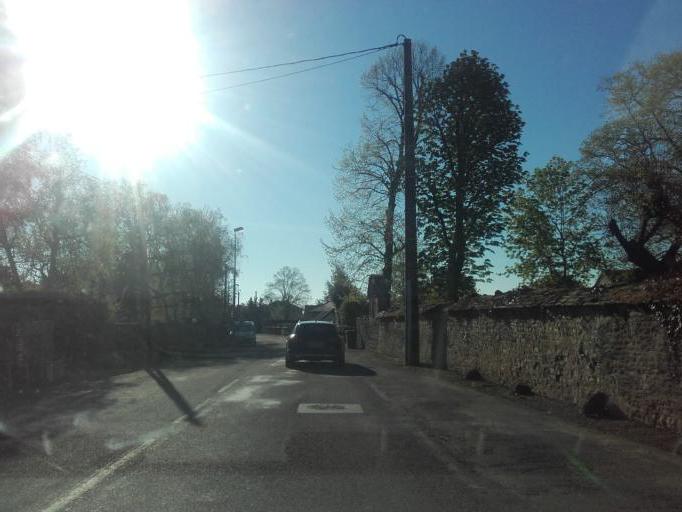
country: FR
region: Bourgogne
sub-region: Departement de Saone-et-Loire
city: Givry
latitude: 46.7847
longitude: 4.7477
